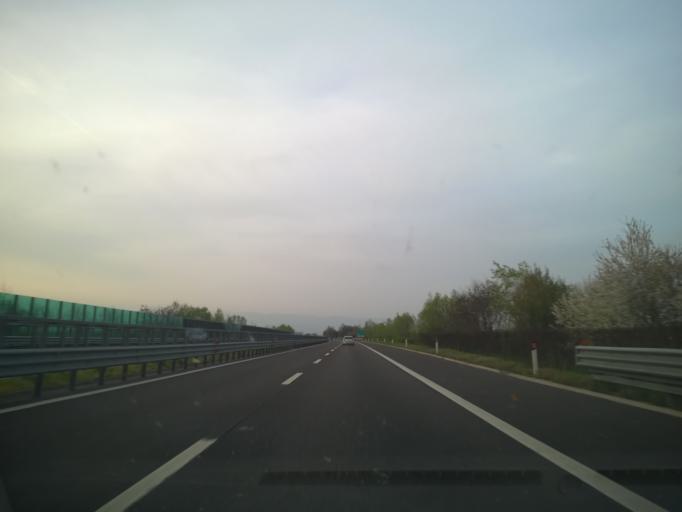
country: IT
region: Veneto
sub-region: Provincia di Vicenza
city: Villaggio Montegrappa
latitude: 45.5586
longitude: 11.6151
